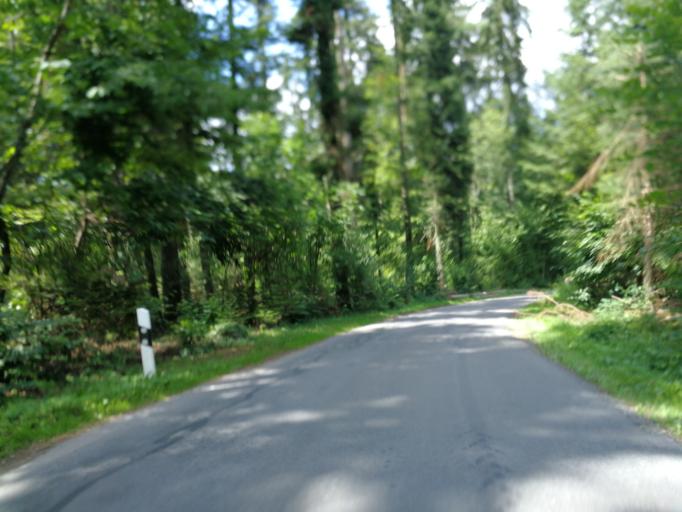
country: CH
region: Zurich
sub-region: Bezirk Hinwil
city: Gruet
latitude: 47.2834
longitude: 8.7878
